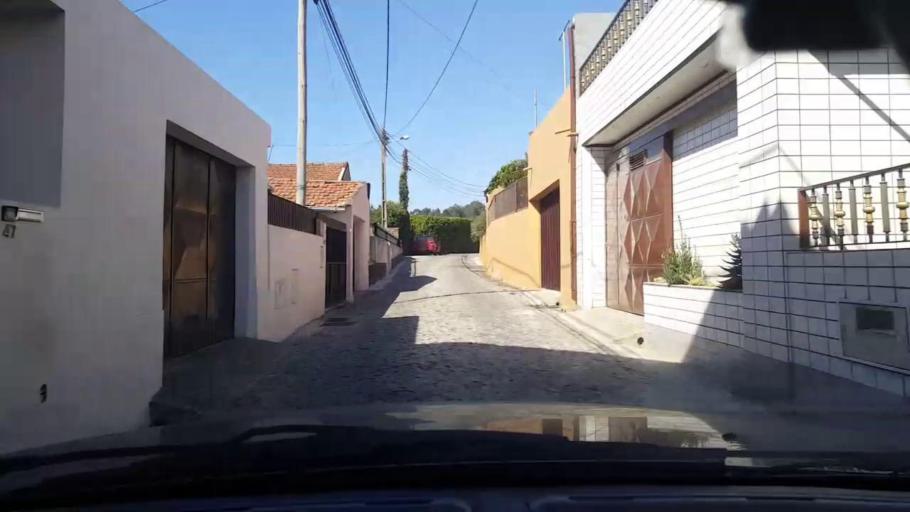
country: PT
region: Porto
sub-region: Matosinhos
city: Lavra
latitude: 41.2978
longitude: -8.7248
